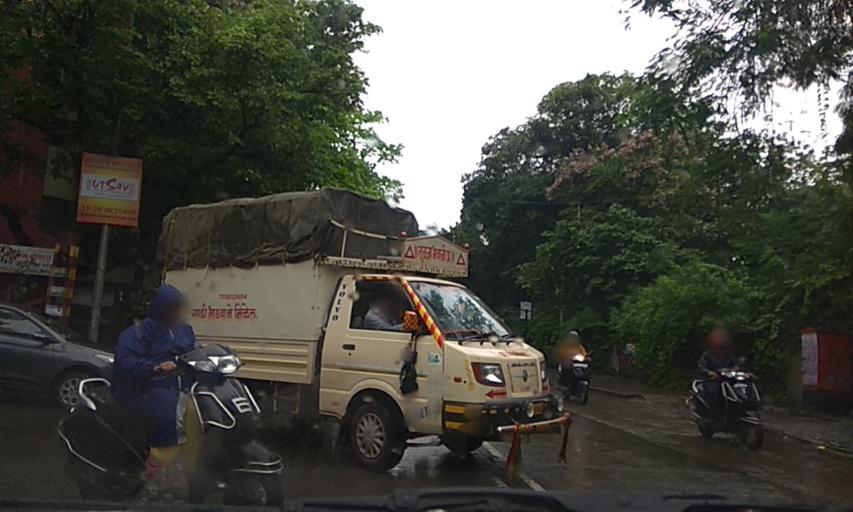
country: IN
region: Maharashtra
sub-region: Pune Division
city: Shivaji Nagar
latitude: 18.5409
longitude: 73.8365
